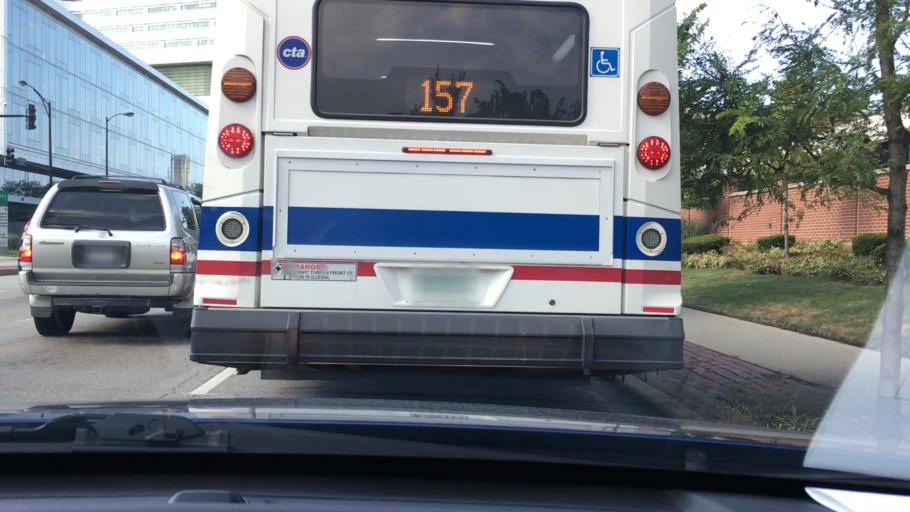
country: US
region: Illinois
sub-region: Cook County
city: Chicago
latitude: 41.8725
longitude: -87.6664
